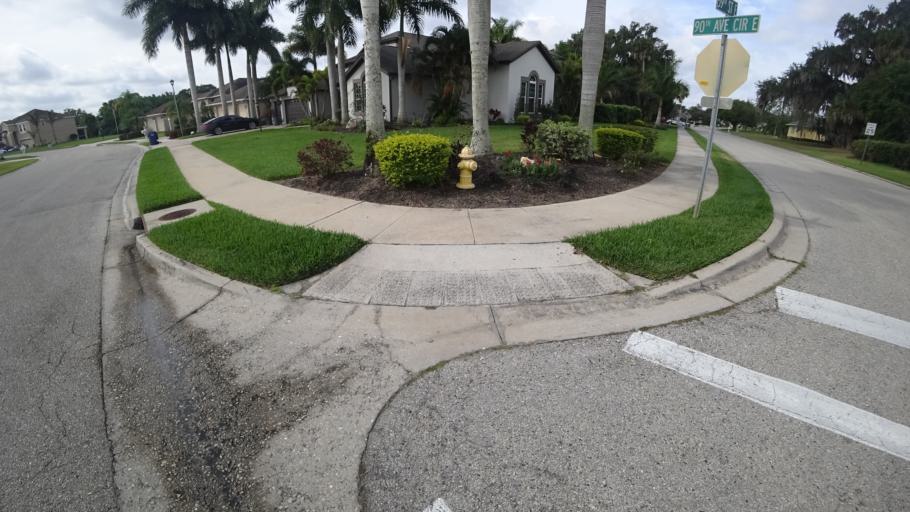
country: US
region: Florida
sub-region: Manatee County
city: Ellenton
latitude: 27.5672
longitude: -82.4735
